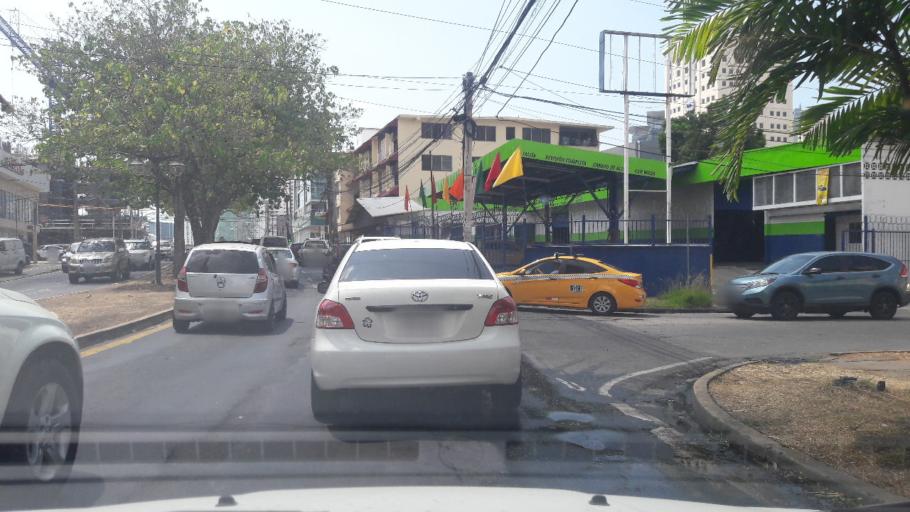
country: PA
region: Panama
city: Panama
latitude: 8.9926
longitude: -79.5229
